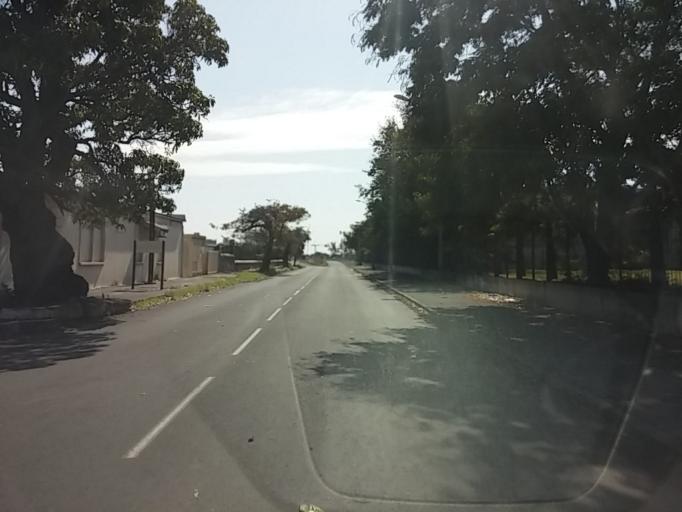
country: RE
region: Reunion
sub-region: Reunion
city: Le Port
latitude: -20.9343
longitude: 55.2898
